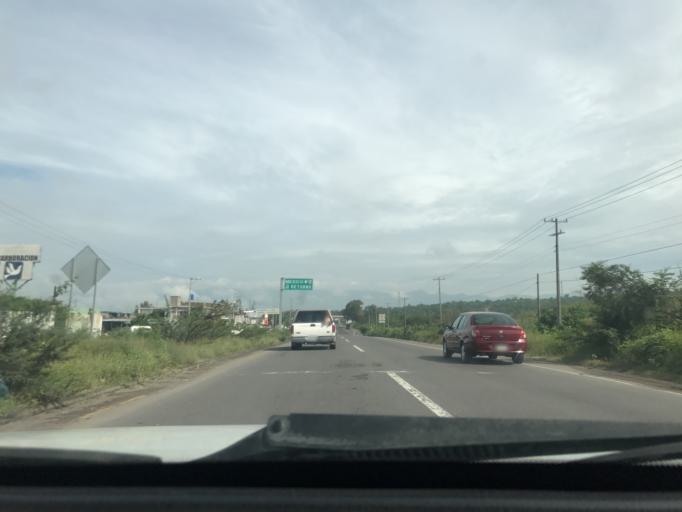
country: MX
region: Morelos
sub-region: Yecapixtla
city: Juan Morales
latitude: 18.8317
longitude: -98.9223
